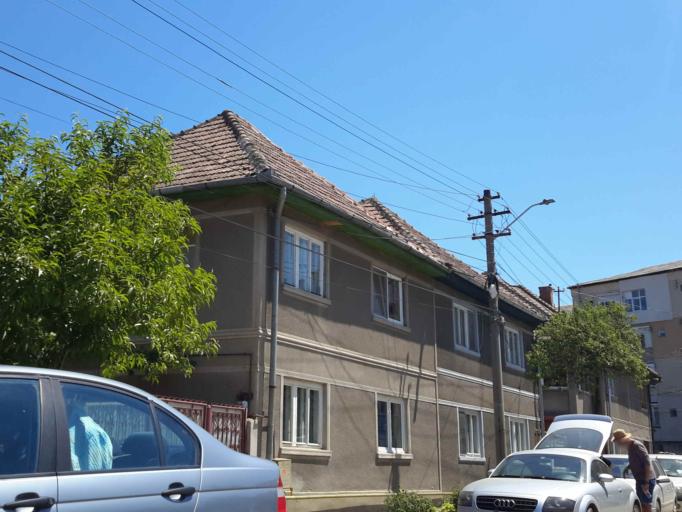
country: RO
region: Alba
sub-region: Municipiul Blaj
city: Veza
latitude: 46.1755
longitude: 23.9287
